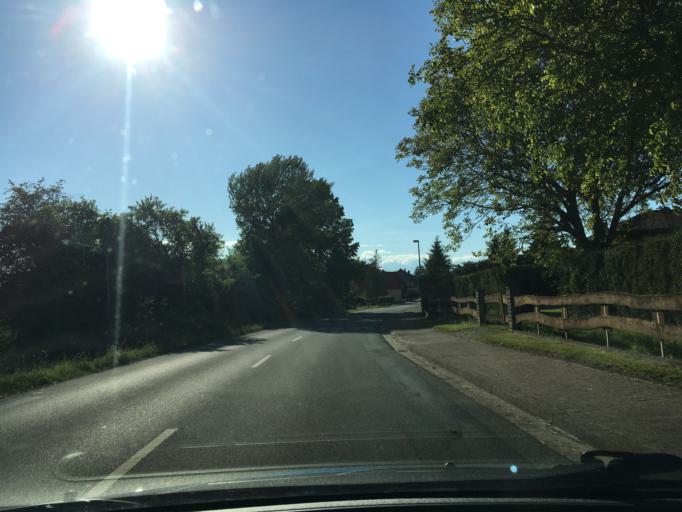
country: DE
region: Lower Saxony
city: Coppengrave
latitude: 51.9881
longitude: 9.7258
